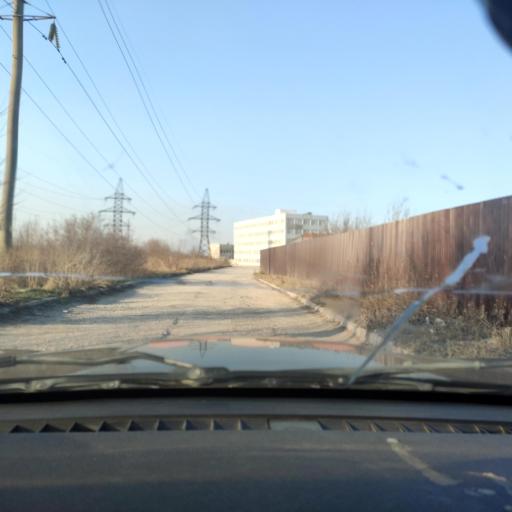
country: RU
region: Samara
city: Tol'yatti
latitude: 53.5818
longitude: 49.2701
